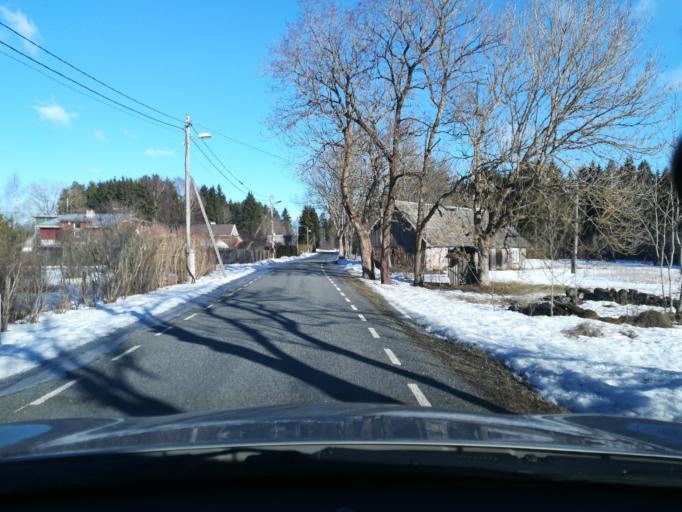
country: EE
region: Raplamaa
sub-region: Kohila vald
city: Kohila
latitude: 59.2309
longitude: 24.7618
